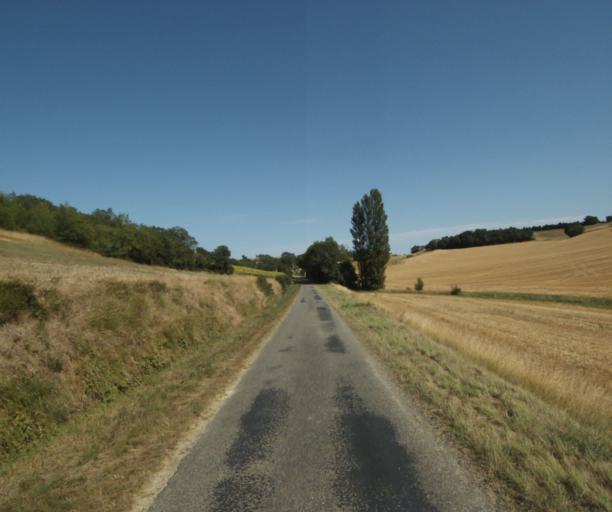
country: FR
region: Midi-Pyrenees
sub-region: Departement de la Haute-Garonne
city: Saint-Felix-Lauragais
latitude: 43.4379
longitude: 1.8383
